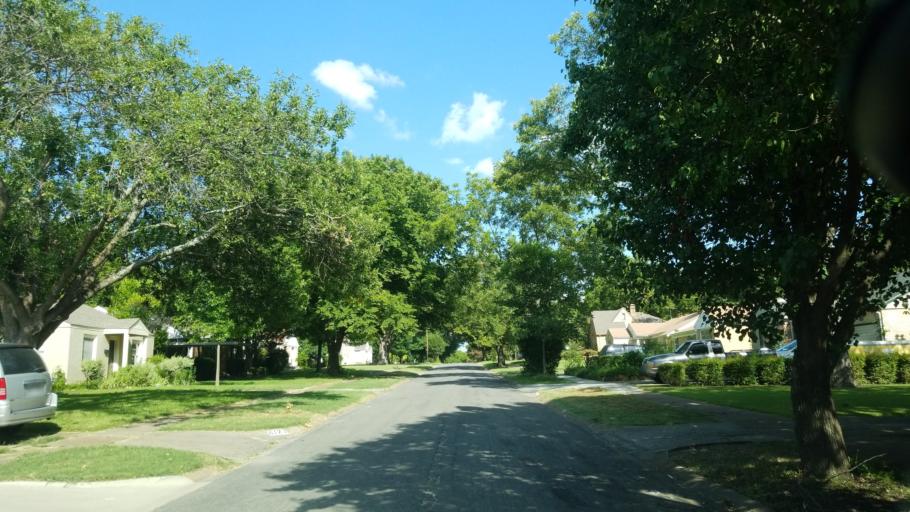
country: US
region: Texas
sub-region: Dallas County
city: Dallas
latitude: 32.7718
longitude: -96.7151
